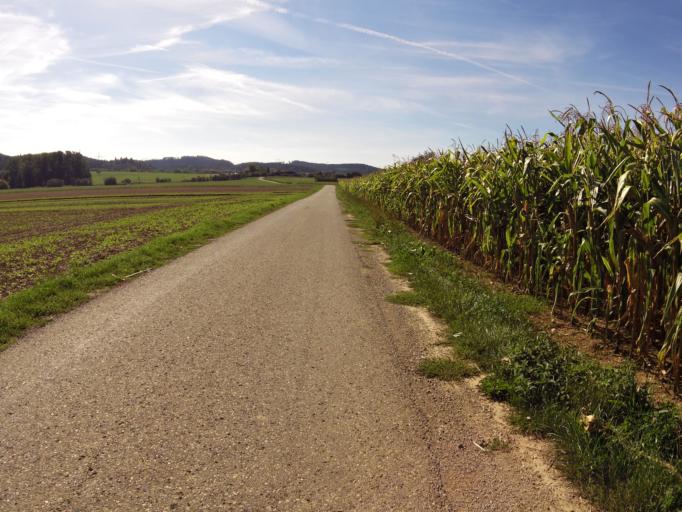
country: DE
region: Baden-Wuerttemberg
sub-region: Freiburg Region
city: Deisslingen
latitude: 48.0973
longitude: 8.5819
